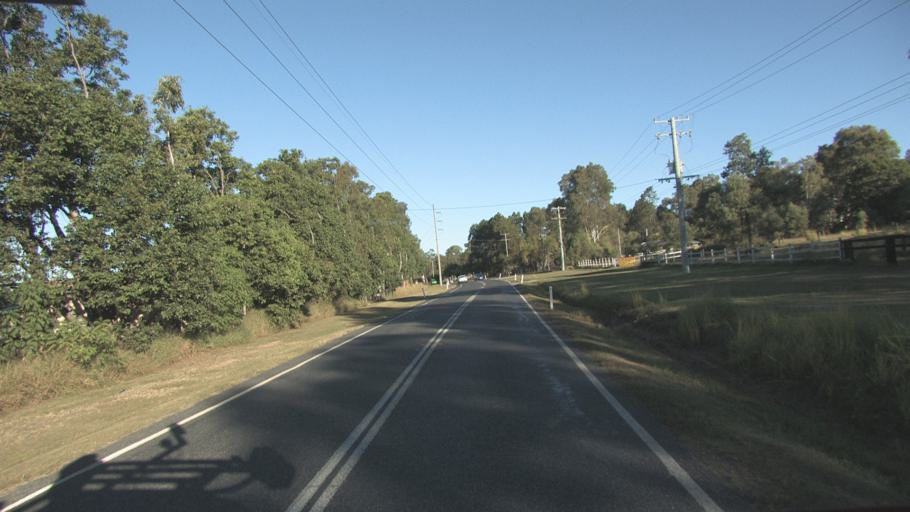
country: AU
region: Queensland
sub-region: Logan
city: Chambers Flat
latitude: -27.7427
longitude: 153.0876
